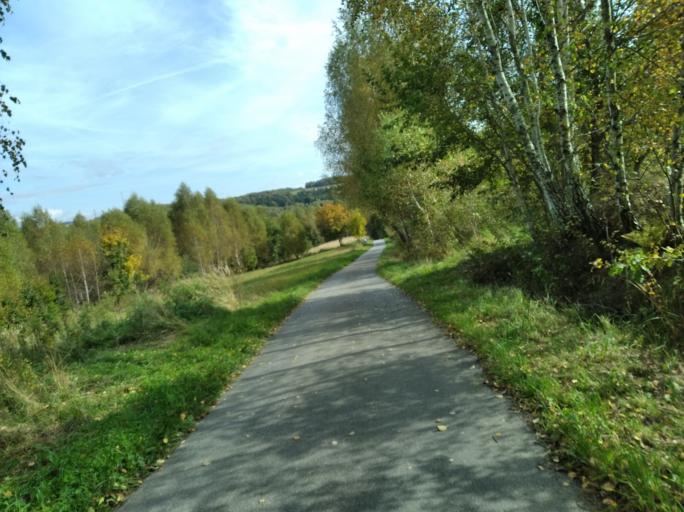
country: PL
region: Subcarpathian Voivodeship
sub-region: Powiat strzyzowski
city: Jawornik
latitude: 49.8375
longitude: 21.8846
